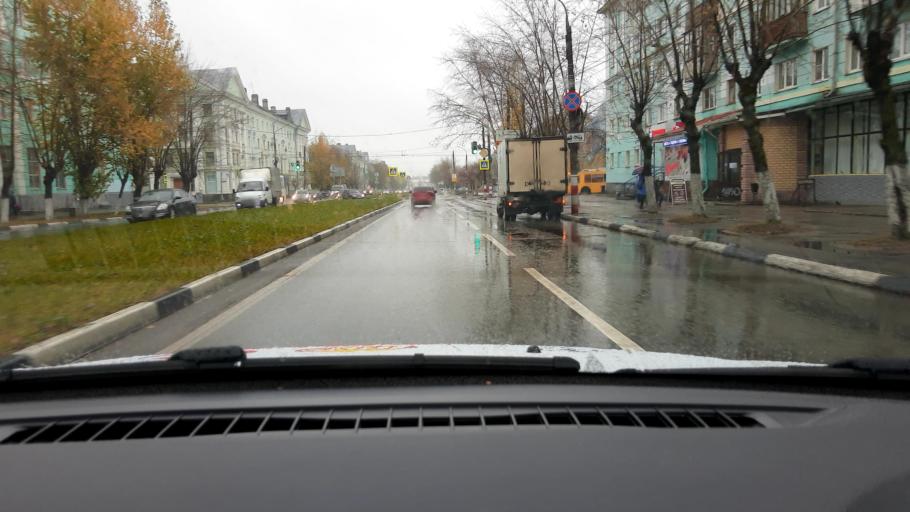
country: RU
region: Nizjnij Novgorod
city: Dzerzhinsk
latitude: 56.2405
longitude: 43.4495
